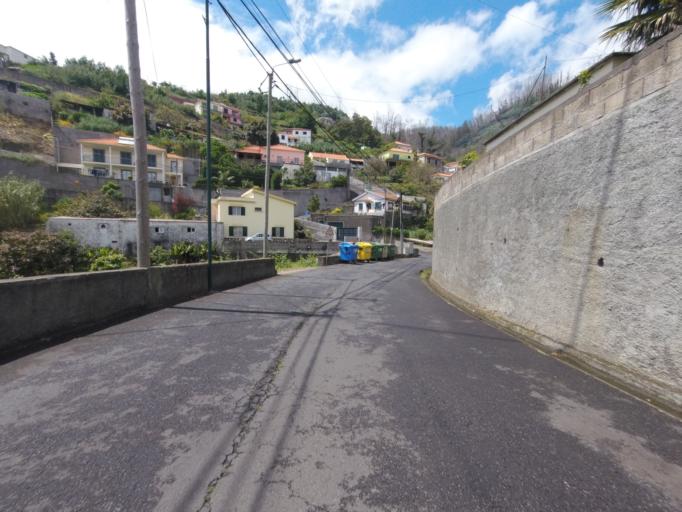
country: PT
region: Madeira
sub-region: Funchal
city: Nossa Senhora do Monte
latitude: 32.6754
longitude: -16.9232
